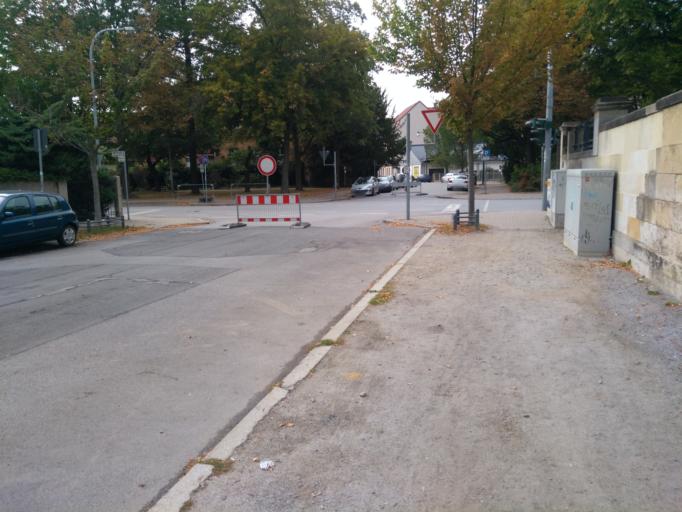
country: DE
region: Saxony
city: Bautzen
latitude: 51.1799
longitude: 14.4340
